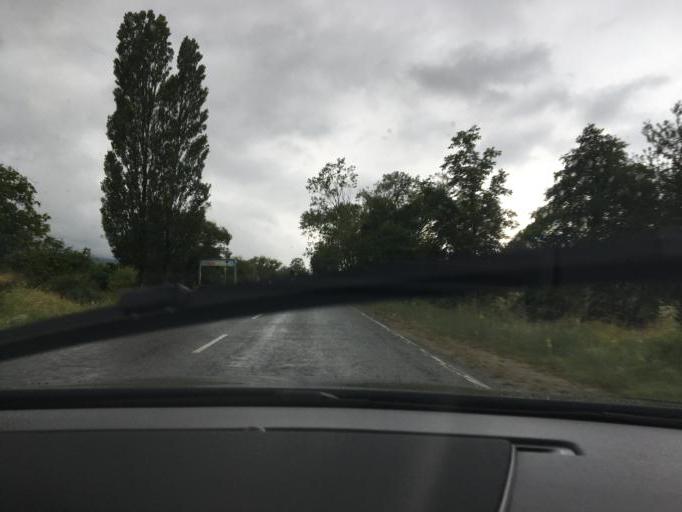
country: BG
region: Kyustendil
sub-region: Obshtina Kyustendil
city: Kyustendil
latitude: 42.2678
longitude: 22.6184
